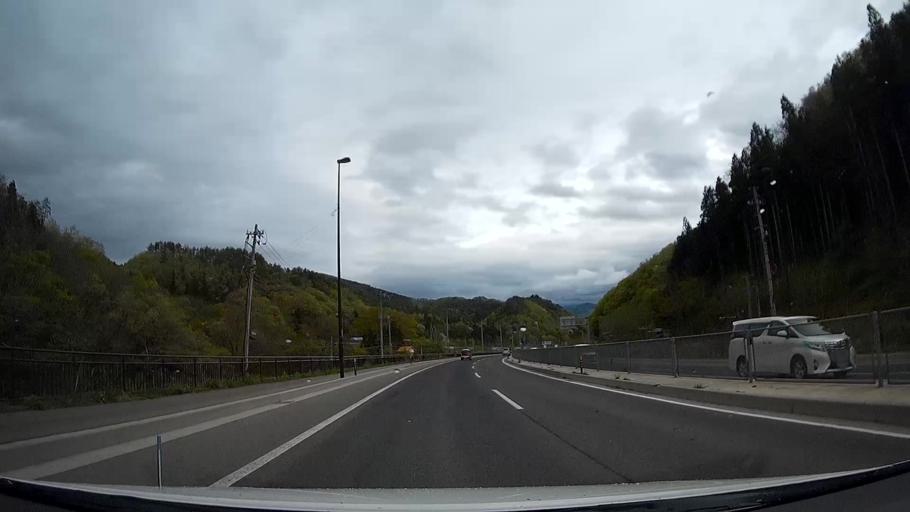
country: JP
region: Yamagata
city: Kaminoyama
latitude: 38.1294
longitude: 140.2216
